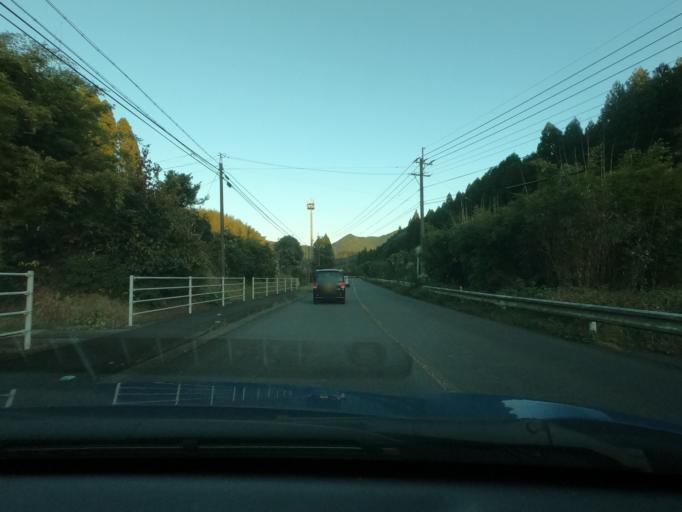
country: JP
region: Kagoshima
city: Satsumasendai
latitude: 31.7963
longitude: 130.4748
